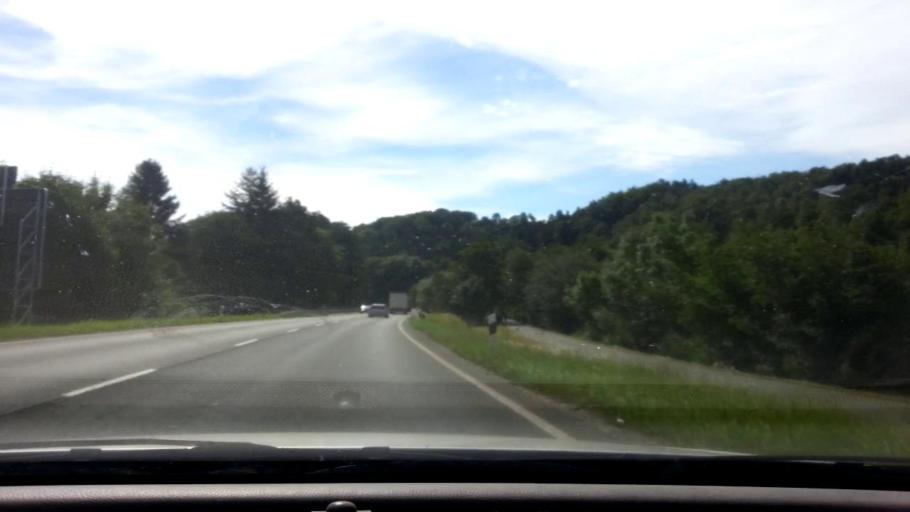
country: DE
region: Bavaria
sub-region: Upper Franconia
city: Bad Berneck im Fichtelgebirge
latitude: 50.0426
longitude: 11.6690
